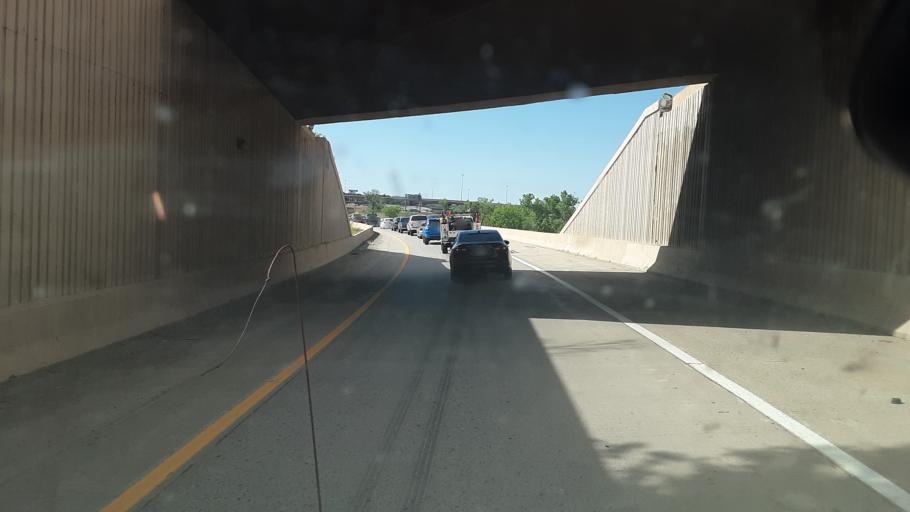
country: US
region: Colorado
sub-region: Adams County
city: Twin Lakes
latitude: 39.8203
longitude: -104.9803
